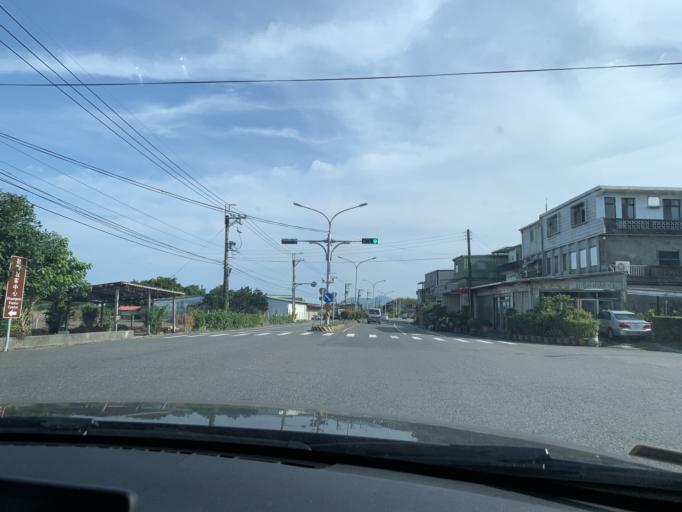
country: TW
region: Taiwan
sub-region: Yilan
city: Yilan
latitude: 24.7357
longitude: 121.8182
